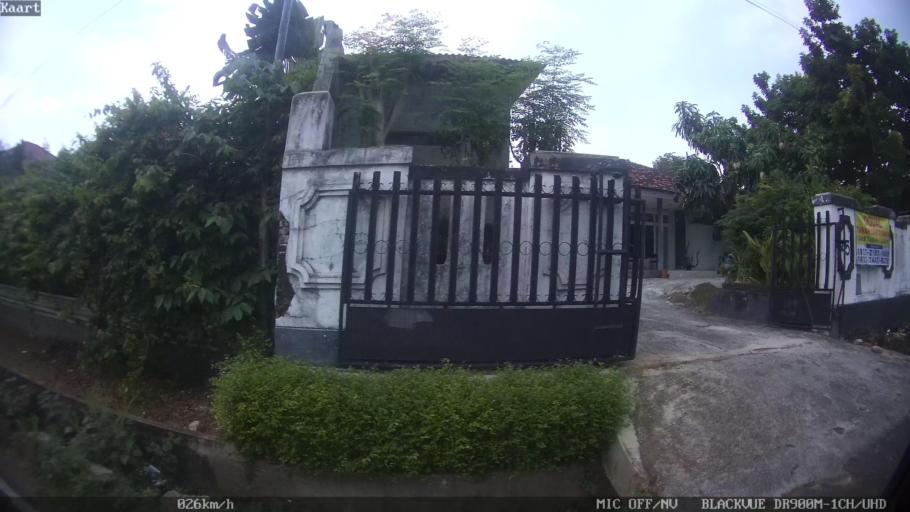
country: ID
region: Lampung
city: Bandarlampung
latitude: -5.4247
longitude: 105.2554
